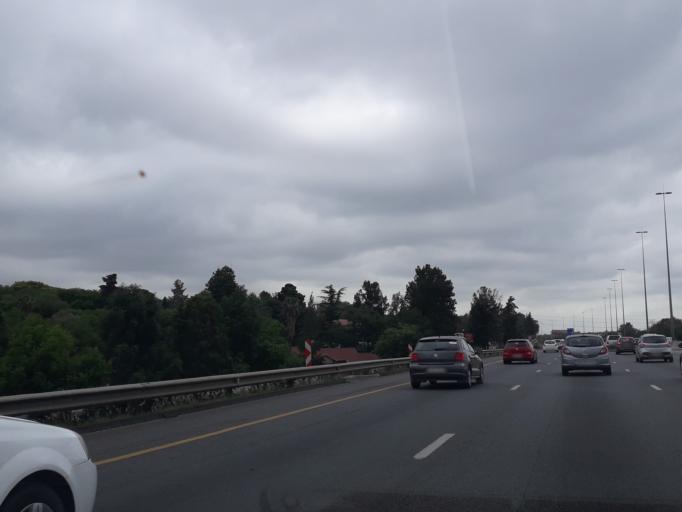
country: ZA
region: Gauteng
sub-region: City of Johannesburg Metropolitan Municipality
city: Roodepoort
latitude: -26.0995
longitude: 27.9641
